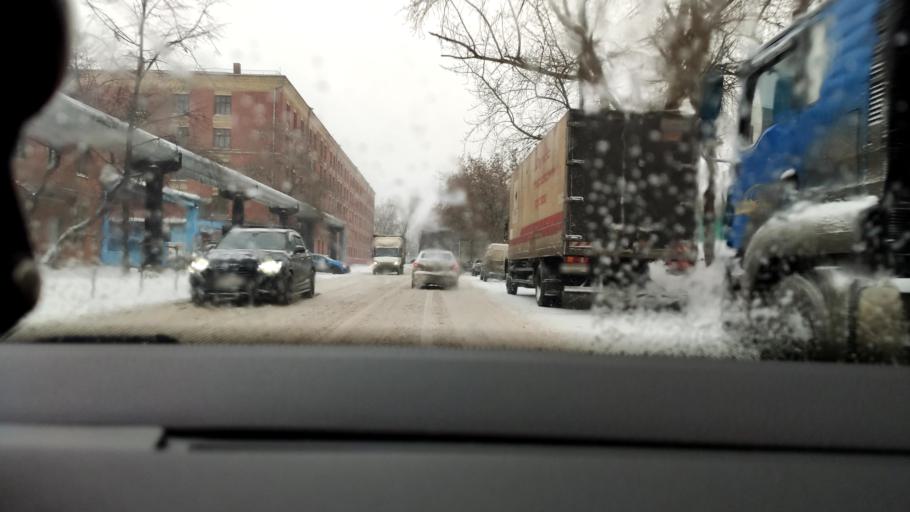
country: RU
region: Moscow
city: Ryazanskiy
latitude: 55.7387
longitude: 37.7485
